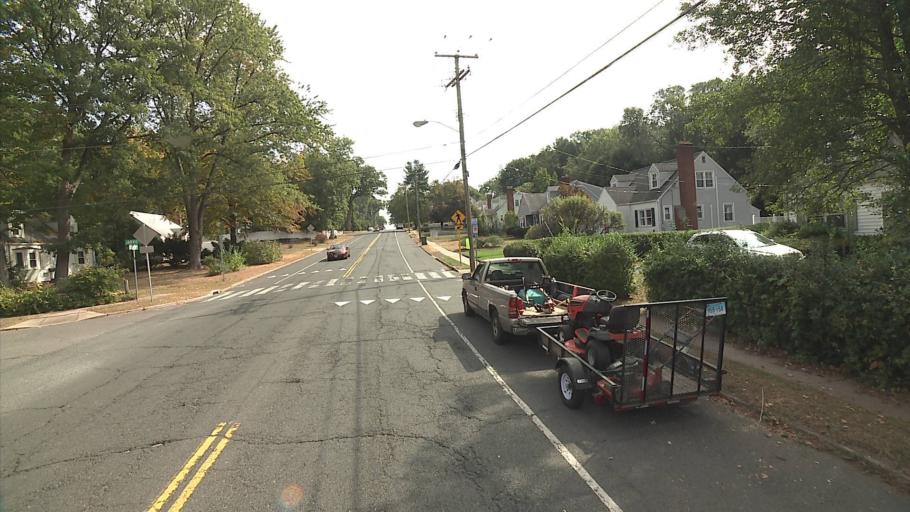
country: US
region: Connecticut
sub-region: Hartford County
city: Manchester
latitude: 41.7780
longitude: -72.5538
